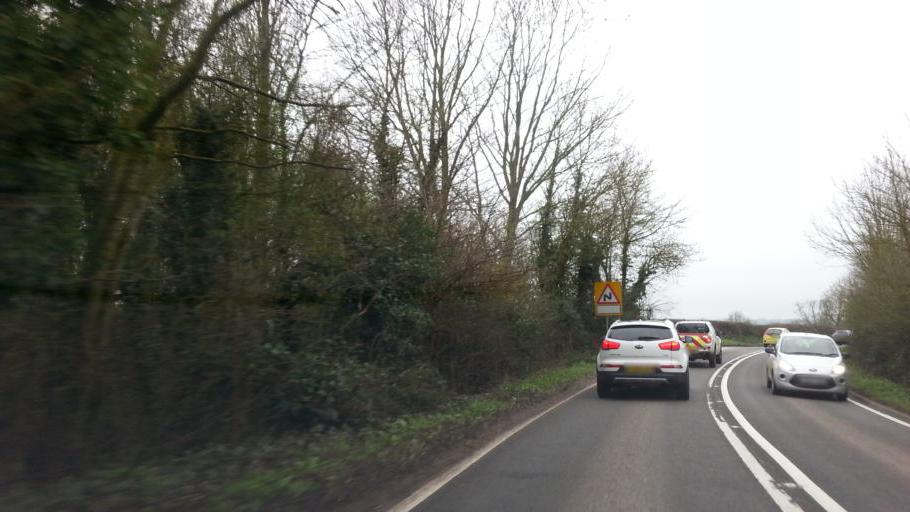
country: GB
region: England
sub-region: Northamptonshire
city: Brackley
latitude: 52.0543
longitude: -1.2237
